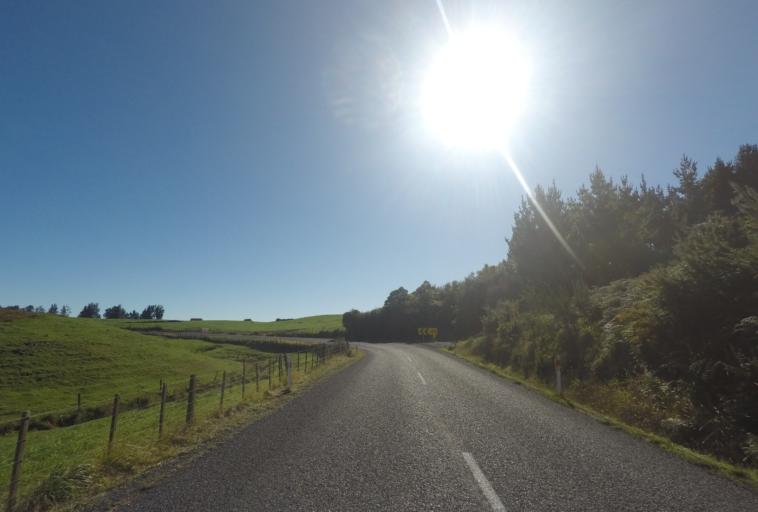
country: NZ
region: Bay of Plenty
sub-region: Western Bay of Plenty District
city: Waihi Beach
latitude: -37.3890
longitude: 175.9054
